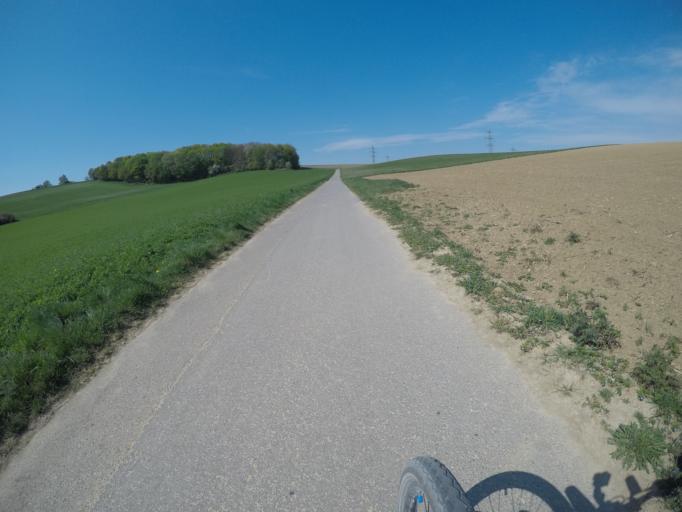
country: DE
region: Baden-Wuerttemberg
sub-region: Regierungsbezirk Stuttgart
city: Ditzingen
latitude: 48.8453
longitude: 9.0497
